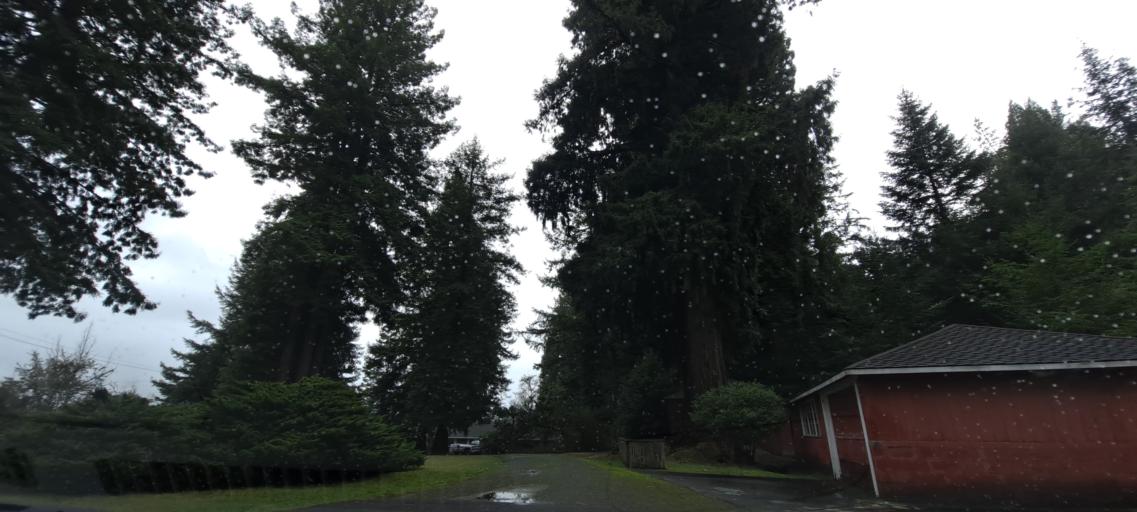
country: US
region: California
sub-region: Humboldt County
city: Fortuna
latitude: 40.6001
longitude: -124.1437
